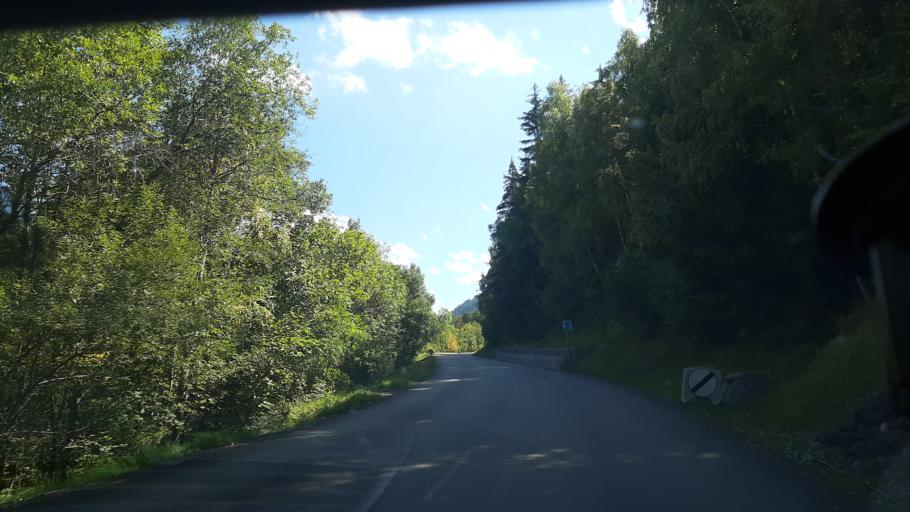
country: FR
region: Rhone-Alpes
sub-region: Departement de la Savoie
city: Saint-Michel-de-Maurienne
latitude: 45.1962
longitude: 6.4654
